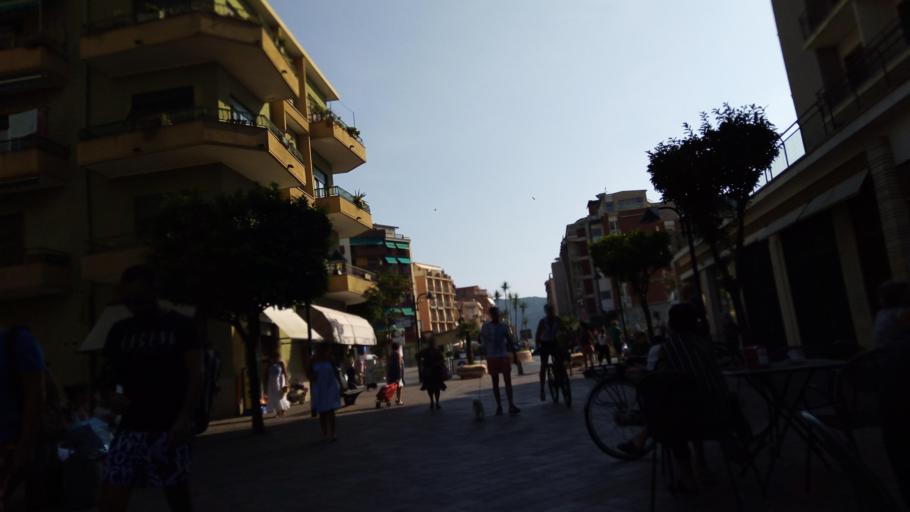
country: IT
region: Liguria
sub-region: Provincia di Savona
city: Pietra Ligure
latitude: 44.1501
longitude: 8.2860
